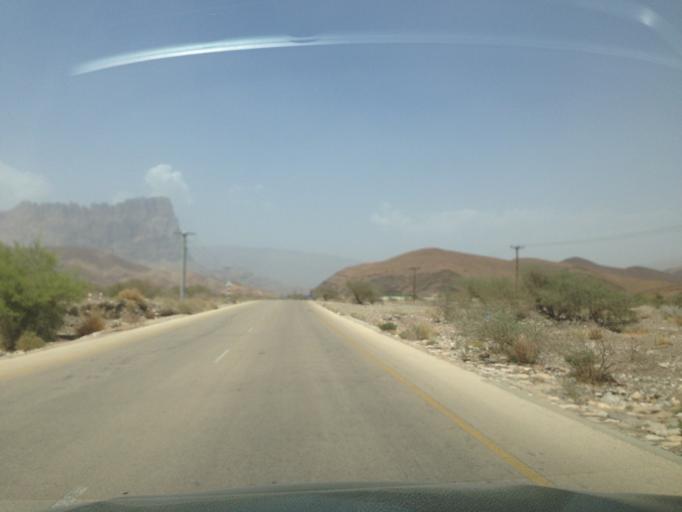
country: OM
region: Az Zahirah
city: `Ibri
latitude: 23.1959
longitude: 56.9335
